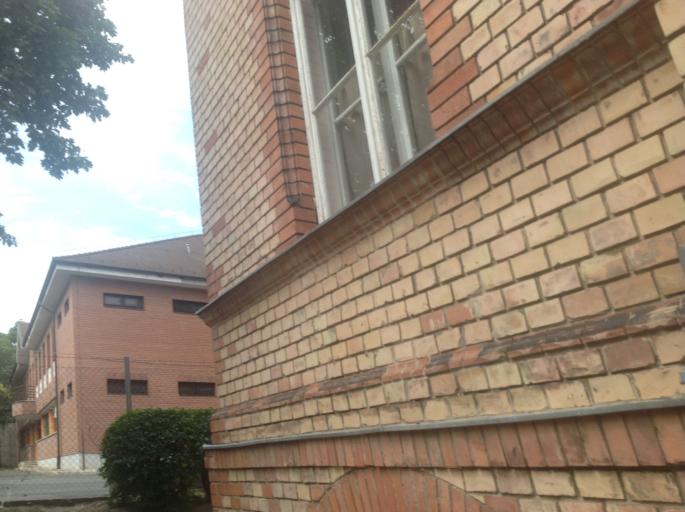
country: HU
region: Budapest
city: Budapest XII. keruelet
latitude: 47.5083
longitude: 19.0043
